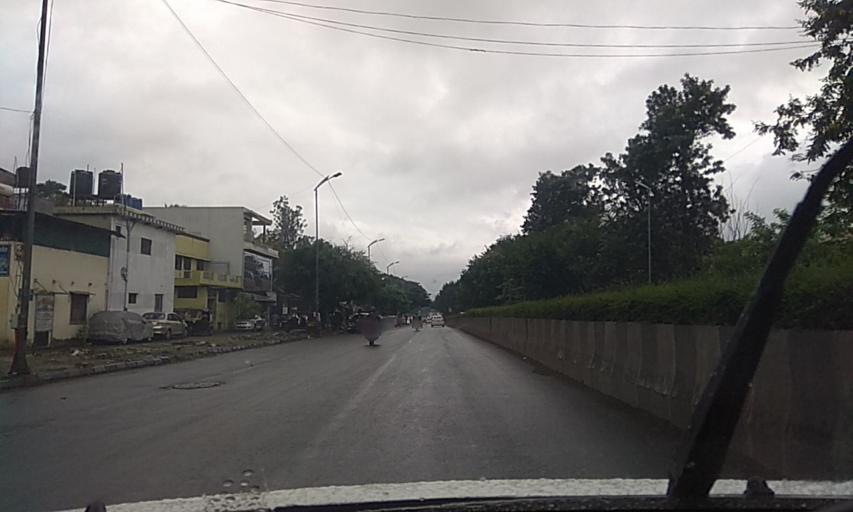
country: IN
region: Maharashtra
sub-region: Pune Division
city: Khadki
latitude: 18.5532
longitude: 73.8818
